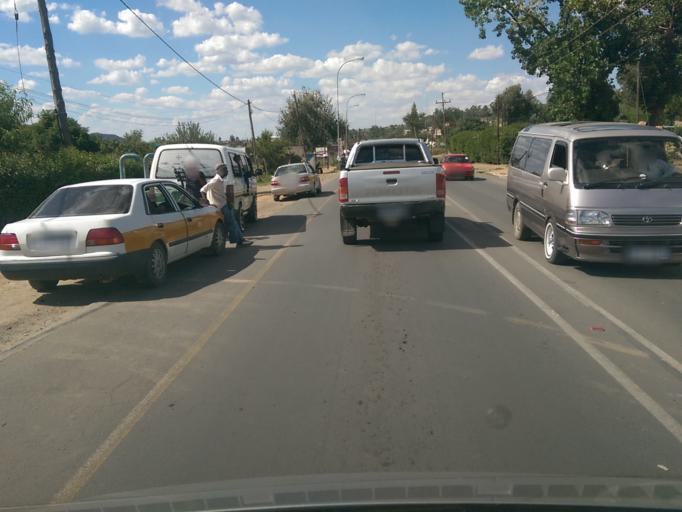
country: LS
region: Maseru
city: Maseru
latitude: -29.3092
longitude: 27.5133
